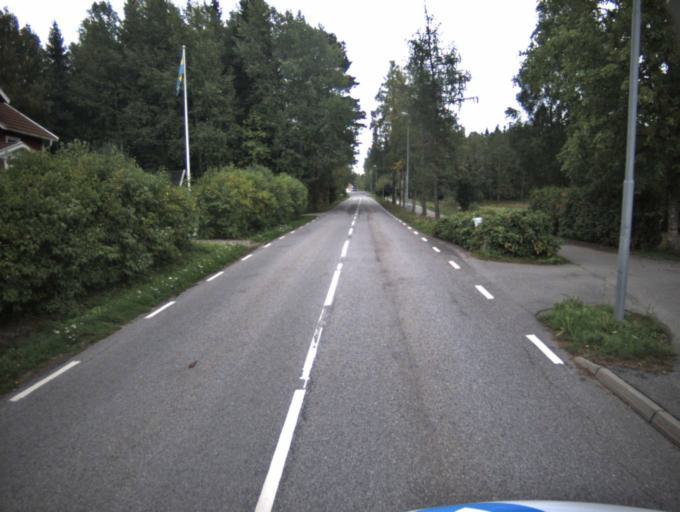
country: SE
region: Vaestra Goetaland
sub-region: Ulricehamns Kommun
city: Ulricehamn
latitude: 57.7767
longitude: 13.4278
